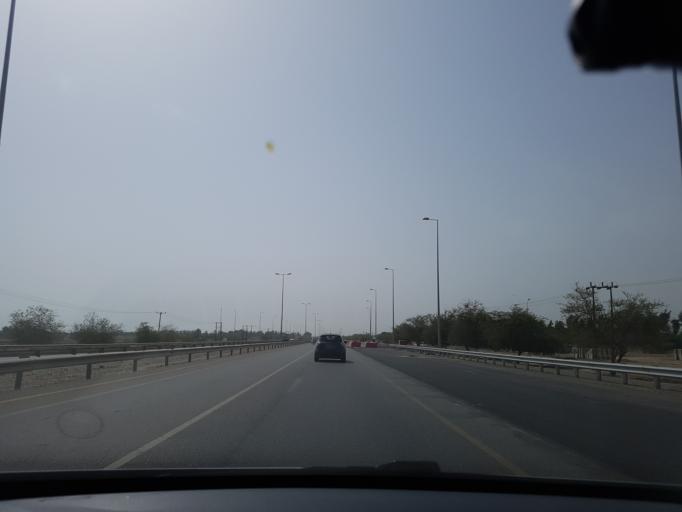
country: OM
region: Al Batinah
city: Al Khaburah
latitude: 23.9989
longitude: 57.0606
